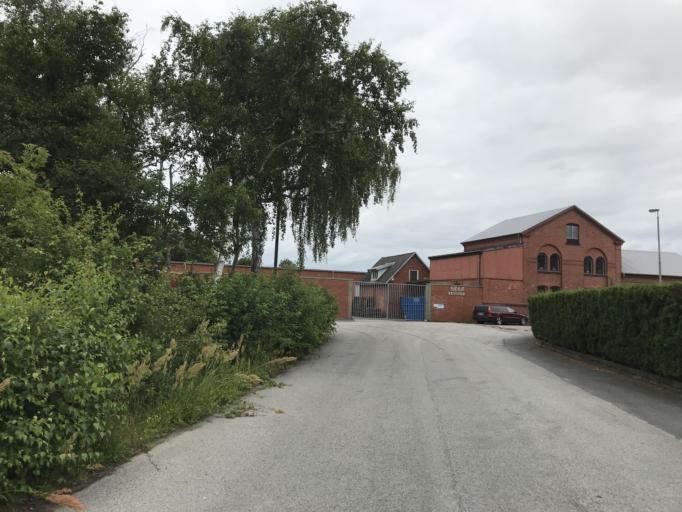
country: SE
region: Skane
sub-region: Burlovs Kommun
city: Arloev
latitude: 55.6191
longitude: 13.0851
